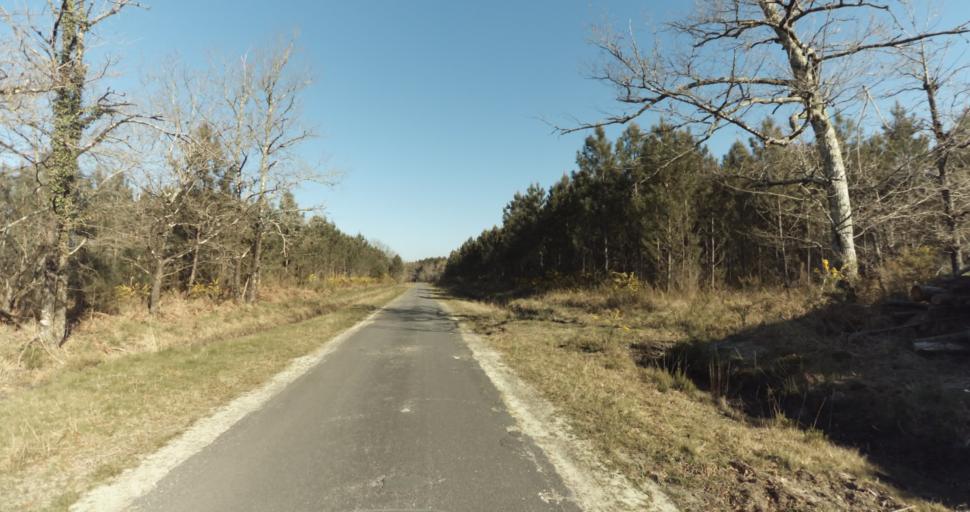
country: FR
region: Aquitaine
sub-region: Departement de la Gironde
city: Martignas-sur-Jalle
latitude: 44.8109
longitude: -0.8526
